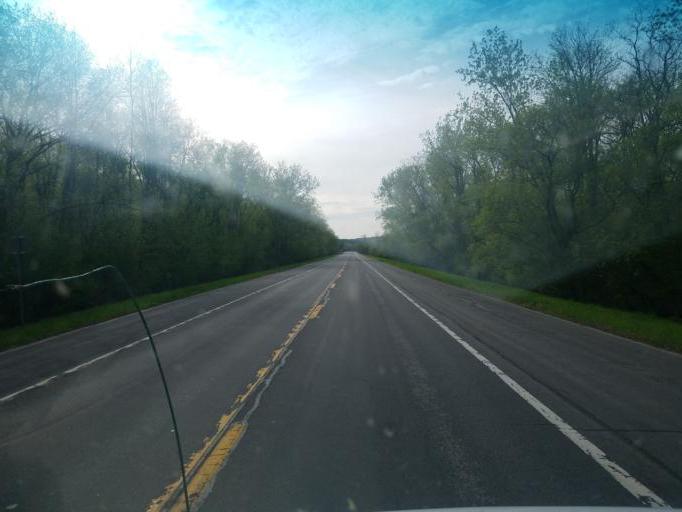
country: US
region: New York
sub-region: Herkimer County
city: Little Falls
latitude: 43.0309
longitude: -74.8242
